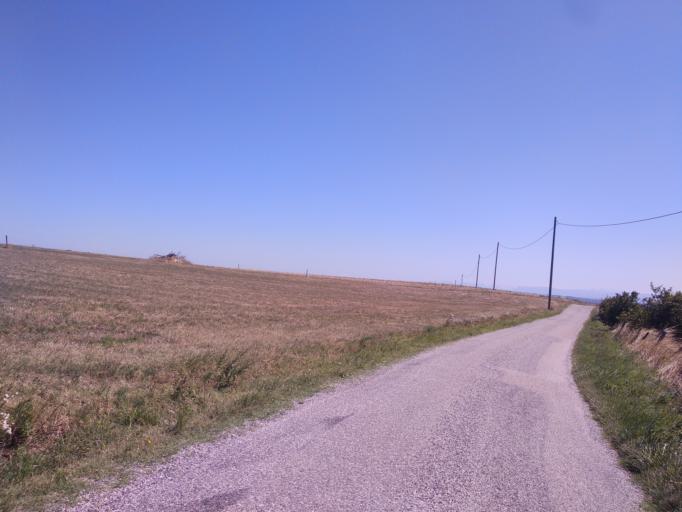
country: FR
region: Rhone-Alpes
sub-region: Departement de l'Ardeche
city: Sarras
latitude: 45.1846
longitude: 4.7708
